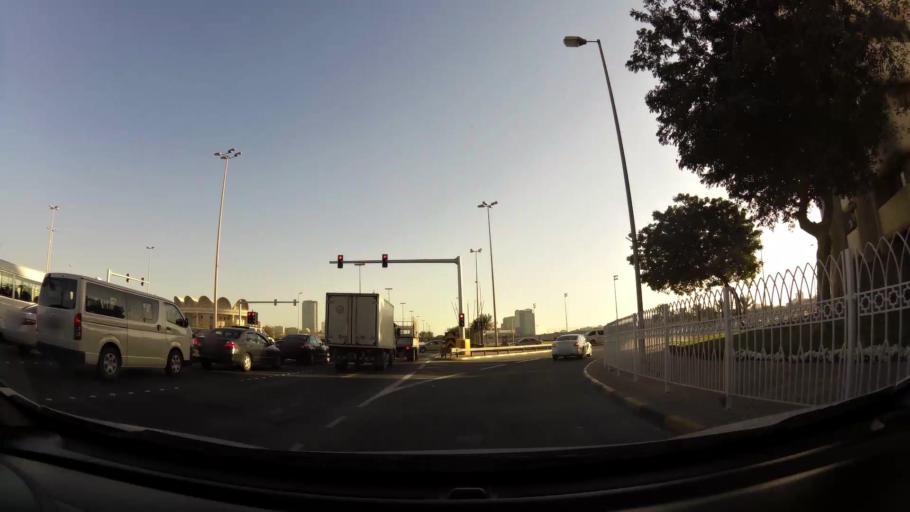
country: BH
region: Manama
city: Manama
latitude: 26.2245
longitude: 50.5980
